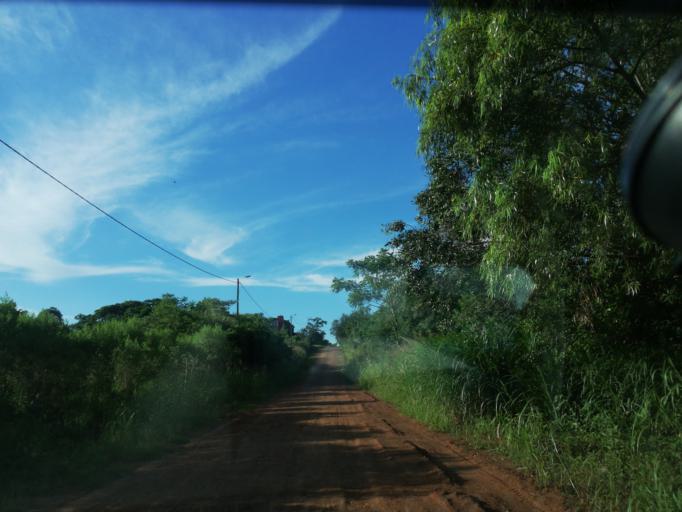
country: AR
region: Misiones
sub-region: Departamento de Capital
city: Posadas
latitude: -27.4018
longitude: -55.9595
